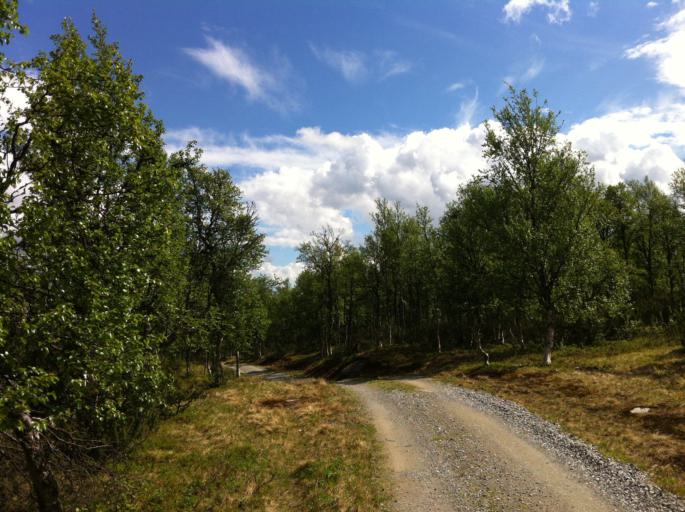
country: NO
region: Sor-Trondelag
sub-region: Tydal
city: Aas
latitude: 62.7079
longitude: 12.4786
